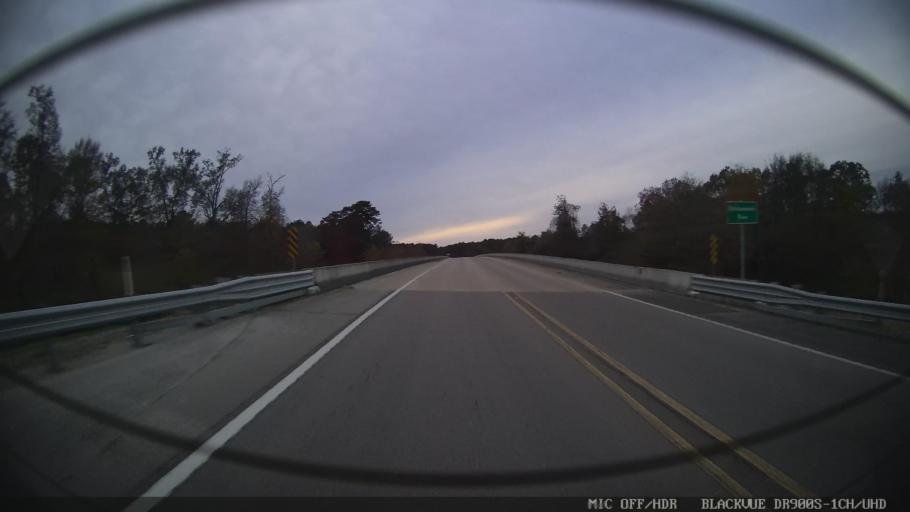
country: US
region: Mississippi
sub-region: Clarke County
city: Quitman
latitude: 32.0420
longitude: -88.7431
